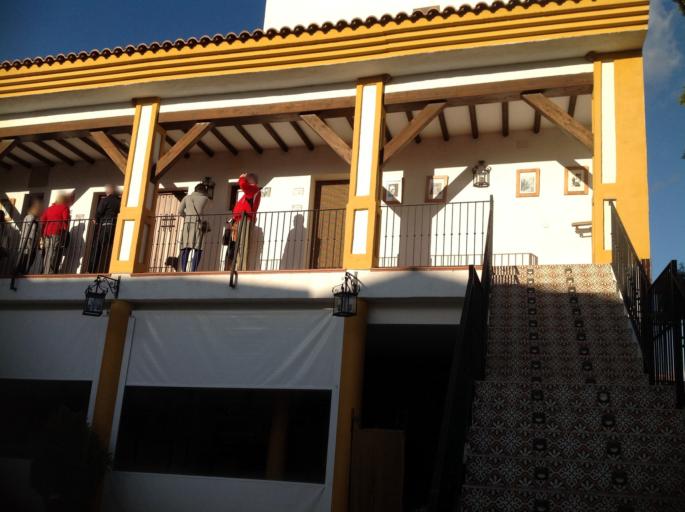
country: ES
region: Andalusia
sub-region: Provincia de Malaga
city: Alameda
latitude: 37.2000
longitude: -4.6409
